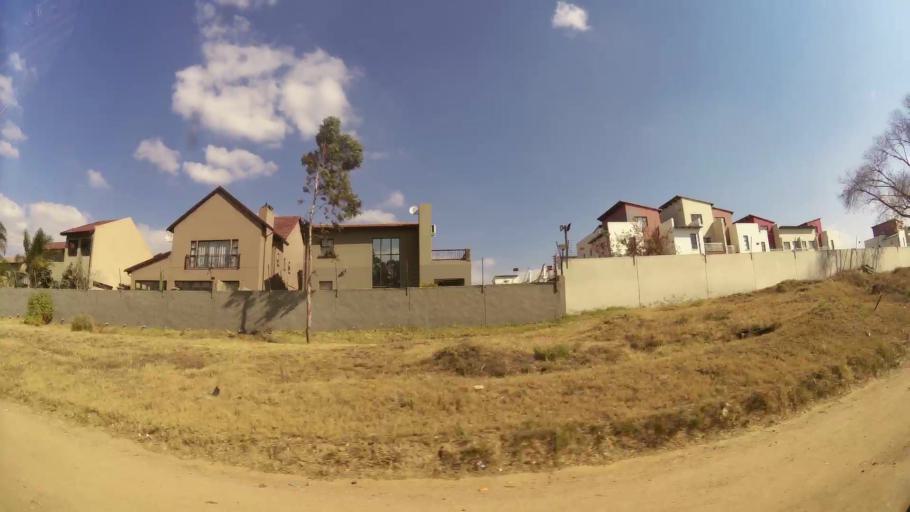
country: ZA
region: Gauteng
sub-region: City of Johannesburg Metropolitan Municipality
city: Midrand
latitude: -26.0107
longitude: 28.0811
